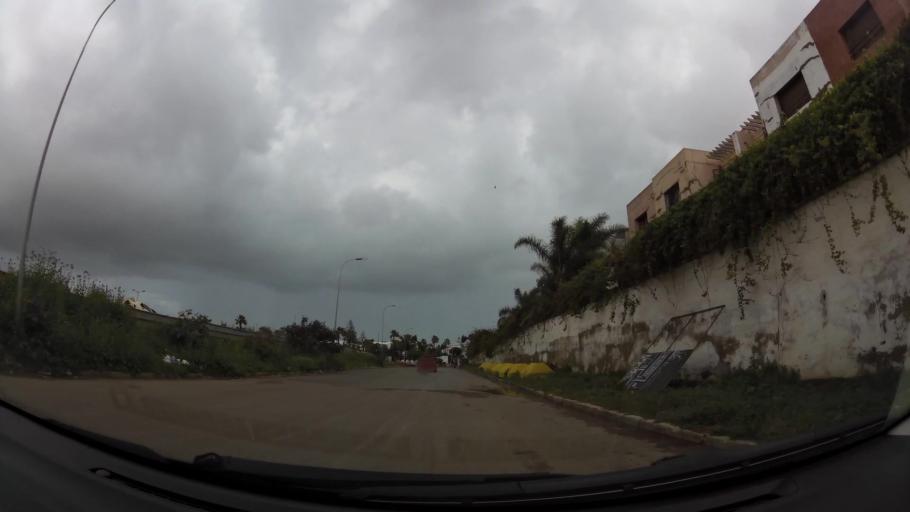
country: MA
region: Grand Casablanca
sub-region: Casablanca
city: Casablanca
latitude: 33.5696
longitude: -7.6893
